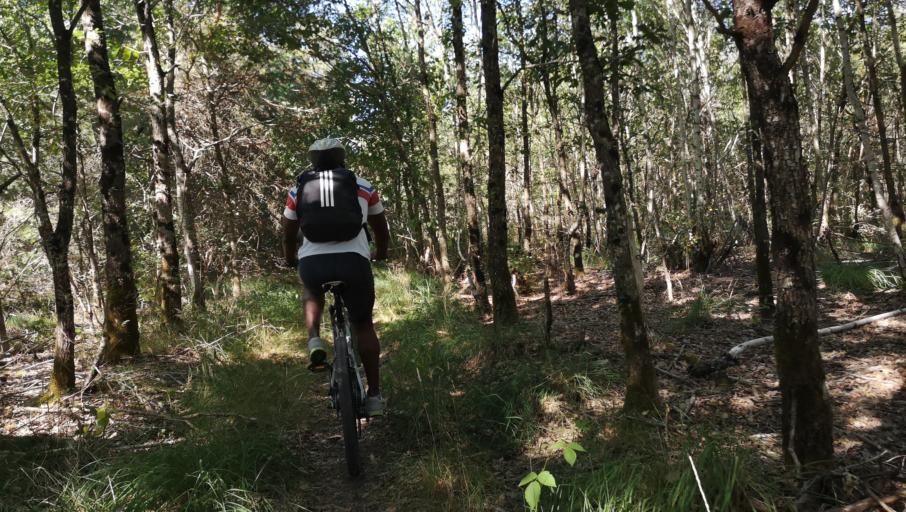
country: FR
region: Centre
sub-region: Departement du Loiret
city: Semoy
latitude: 47.9497
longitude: 1.9562
